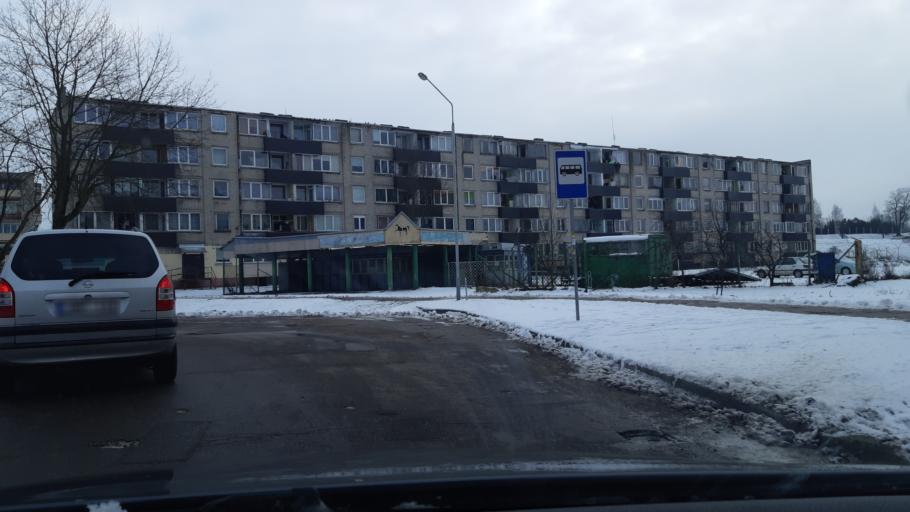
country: LT
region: Kauno apskritis
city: Kedainiai
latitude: 55.2906
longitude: 23.9840
